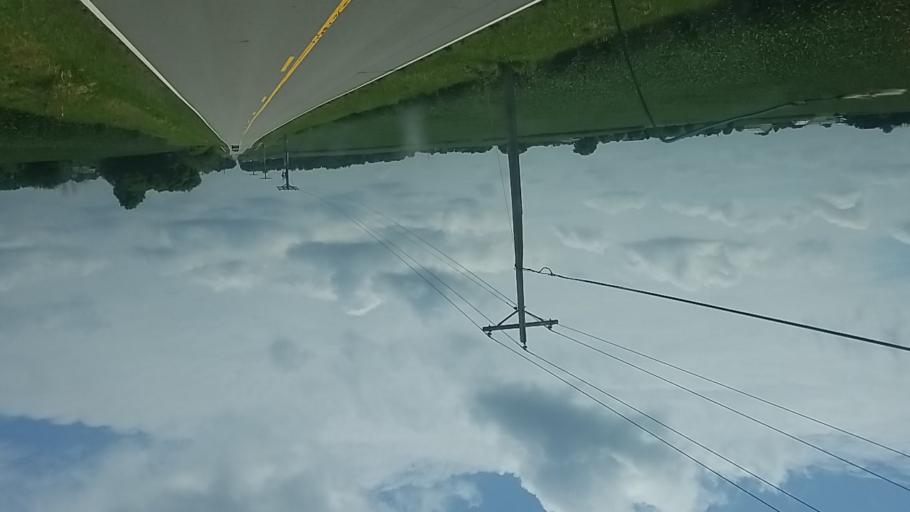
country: US
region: Ohio
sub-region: Fairfield County
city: Lithopolis
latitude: 39.7489
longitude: -82.7852
